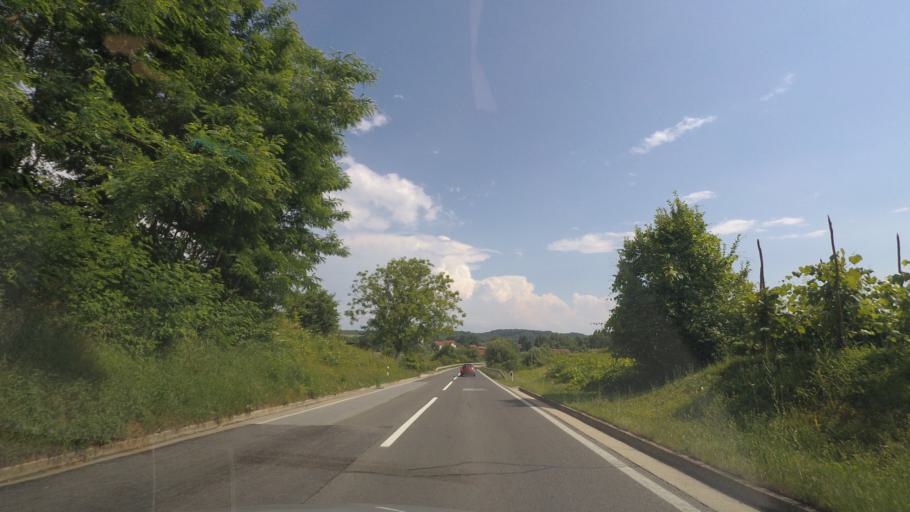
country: HR
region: Karlovacka
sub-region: Grad Karlovac
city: Karlovac
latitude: 45.4393
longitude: 15.4961
